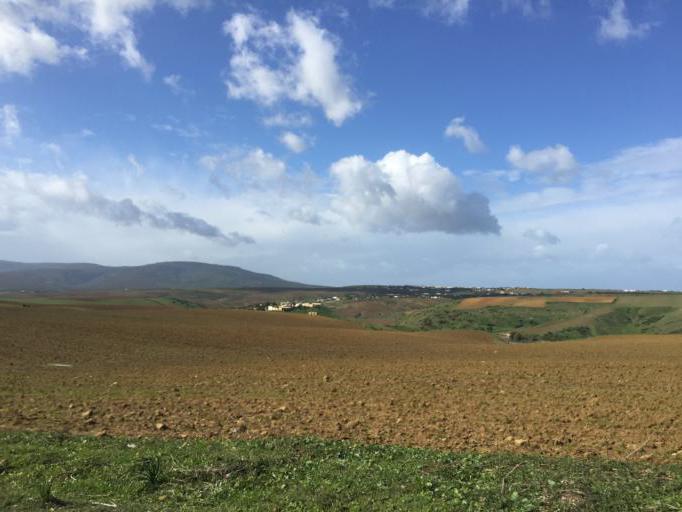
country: TN
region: Nabul
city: El Mida
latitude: 36.8697
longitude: 10.8752
